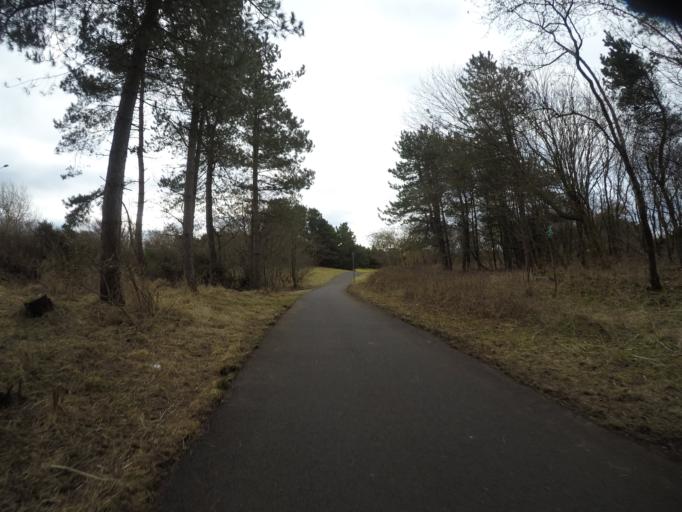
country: GB
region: Scotland
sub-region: North Ayrshire
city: Irvine
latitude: 55.6052
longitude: -4.6808
